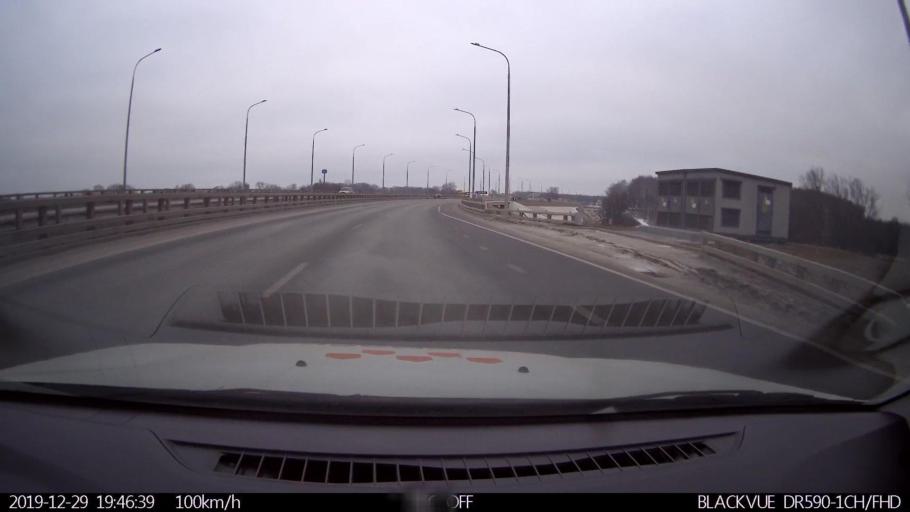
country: RU
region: Nizjnij Novgorod
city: Neklyudovo
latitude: 56.3971
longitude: 43.9924
